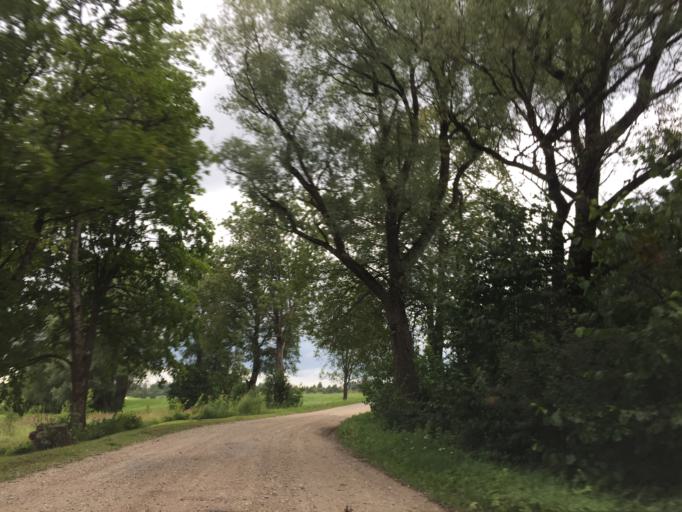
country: LV
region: Seja
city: Loja
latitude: 57.1473
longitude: 24.6609
